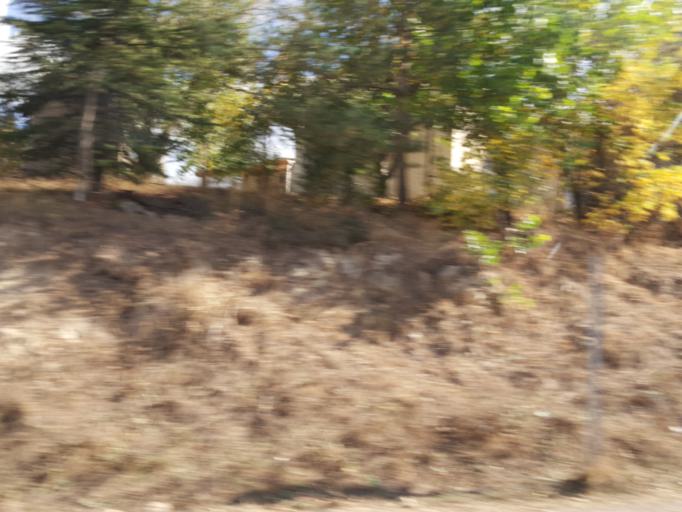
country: TR
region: Tokat
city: Sulusaray
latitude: 40.0057
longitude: 36.1490
